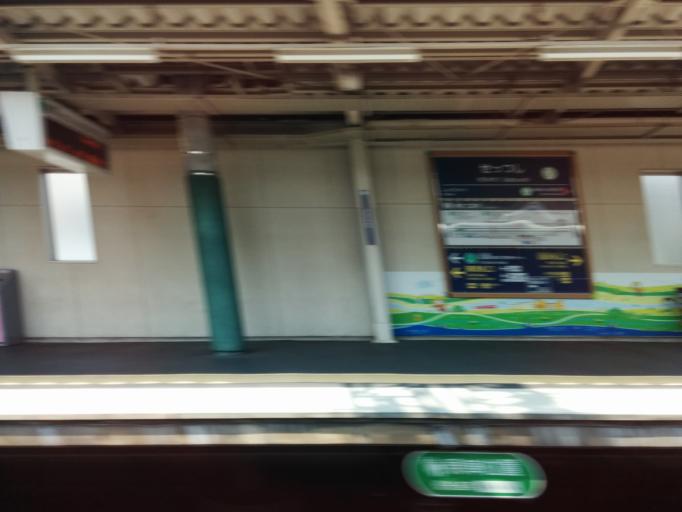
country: JP
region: Osaka
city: Ibaraki
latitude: 34.7868
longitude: 135.5539
